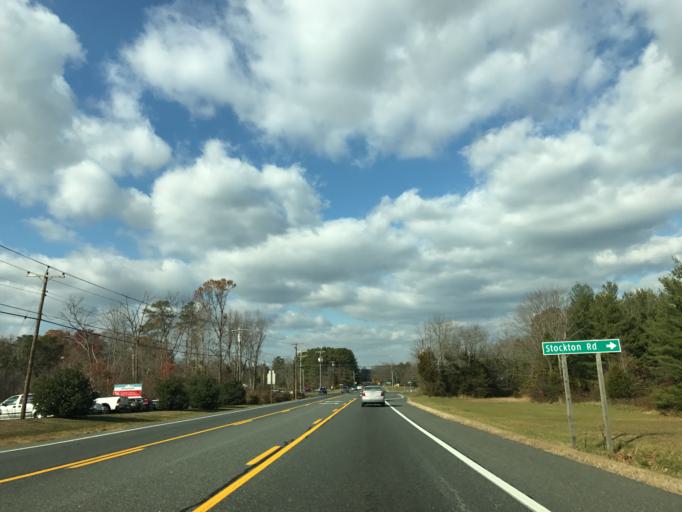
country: US
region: Maryland
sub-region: Harford County
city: Joppatowne
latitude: 39.4700
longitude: -76.3737
